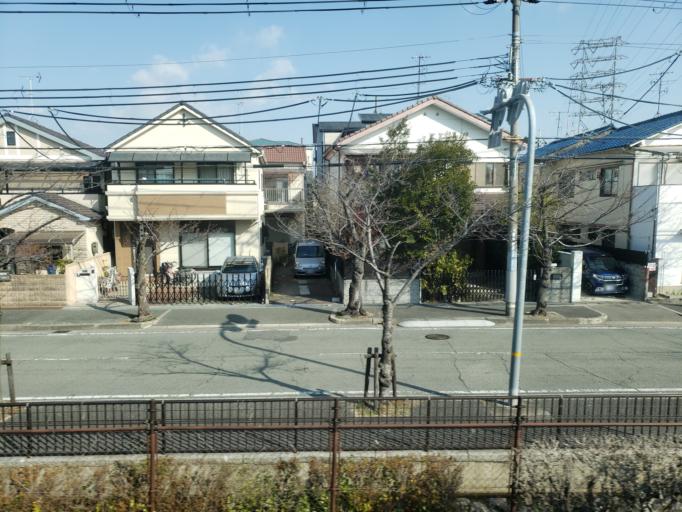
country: JP
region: Hyogo
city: Amagasaki
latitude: 34.7389
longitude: 135.3950
